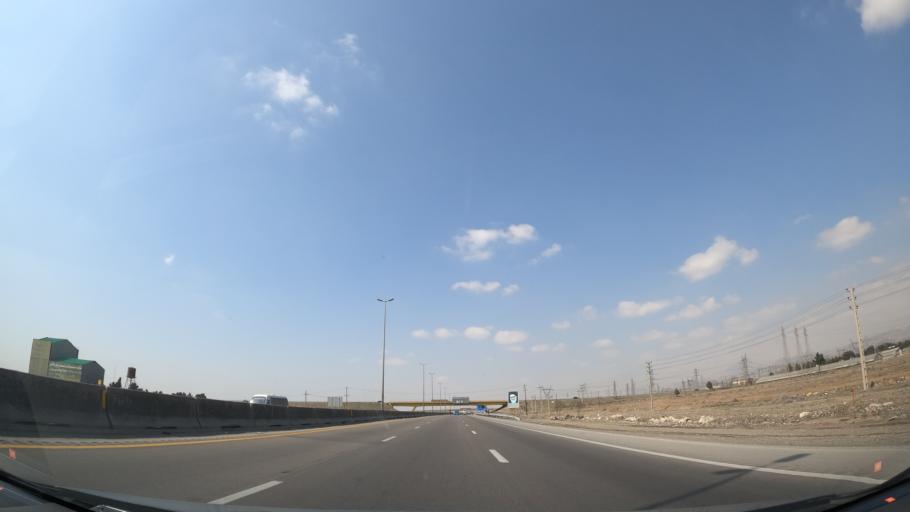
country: IR
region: Qazvin
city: Abyek
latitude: 36.0754
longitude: 50.4700
